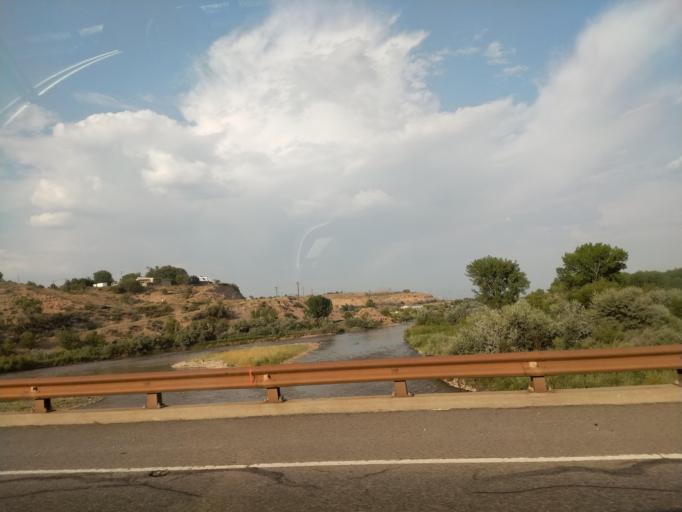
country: US
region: Colorado
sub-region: Garfield County
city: Rifle
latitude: 39.5264
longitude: -107.7785
